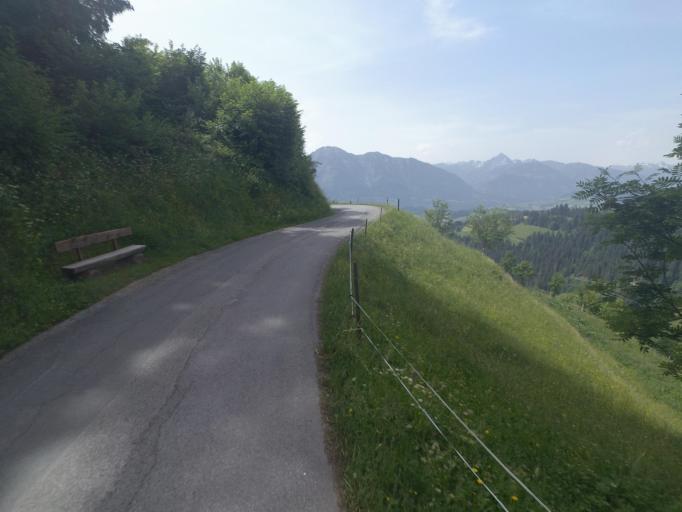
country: AT
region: Salzburg
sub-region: Politischer Bezirk Sankt Johann im Pongau
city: Muhlbach am Hochkonig
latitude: 47.3494
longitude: 13.1200
